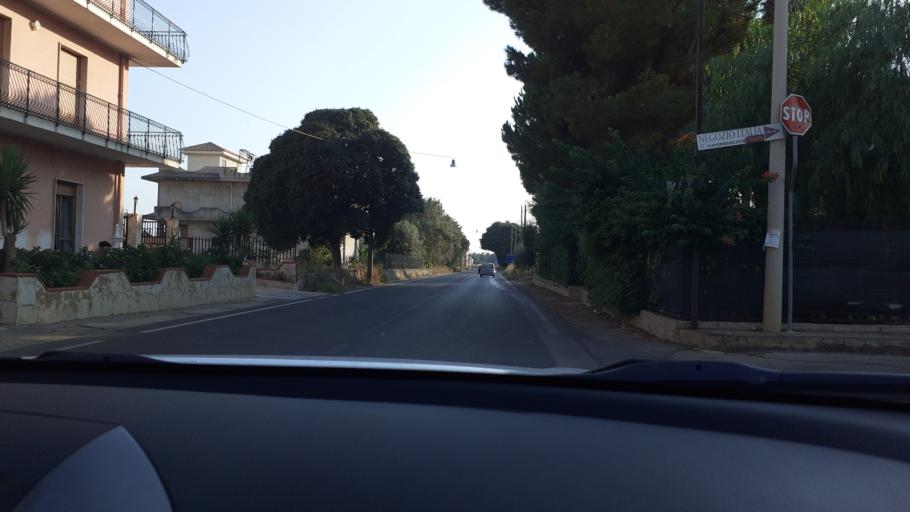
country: IT
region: Sicily
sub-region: Provincia di Siracusa
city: Cassibile
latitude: 36.9748
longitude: 15.1953
